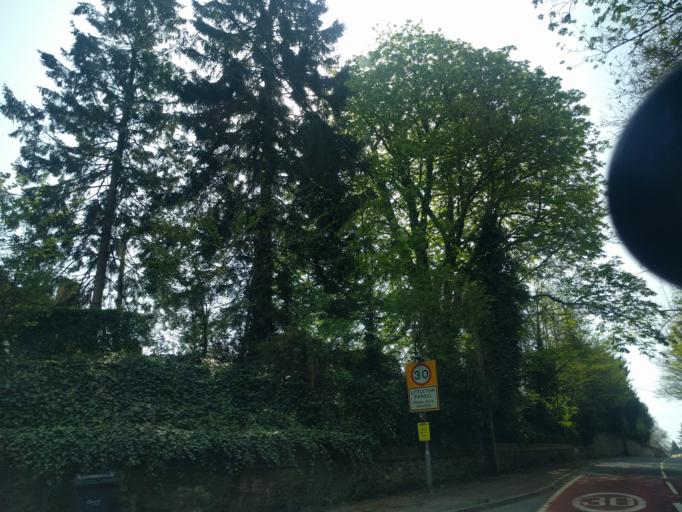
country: GB
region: England
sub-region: Wiltshire
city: Market Lavington
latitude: 51.2890
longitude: -2.0055
